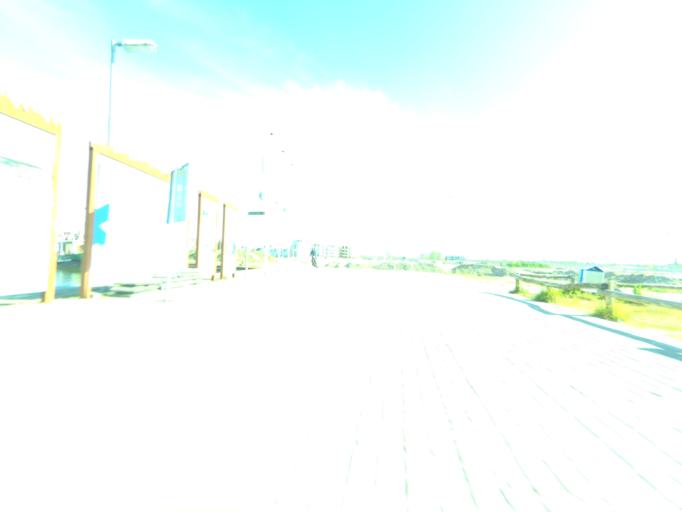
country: NL
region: Gelderland
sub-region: Gemeente Harderwijk
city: Harderwijk
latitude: 52.3538
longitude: 5.6215
